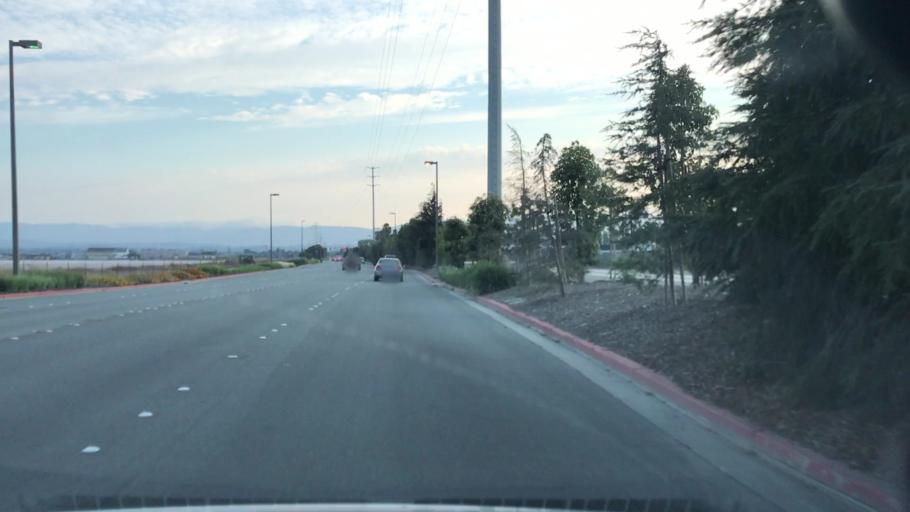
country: US
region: California
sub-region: San Mateo County
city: North Fair Oaks
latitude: 37.5071
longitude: -122.2089
